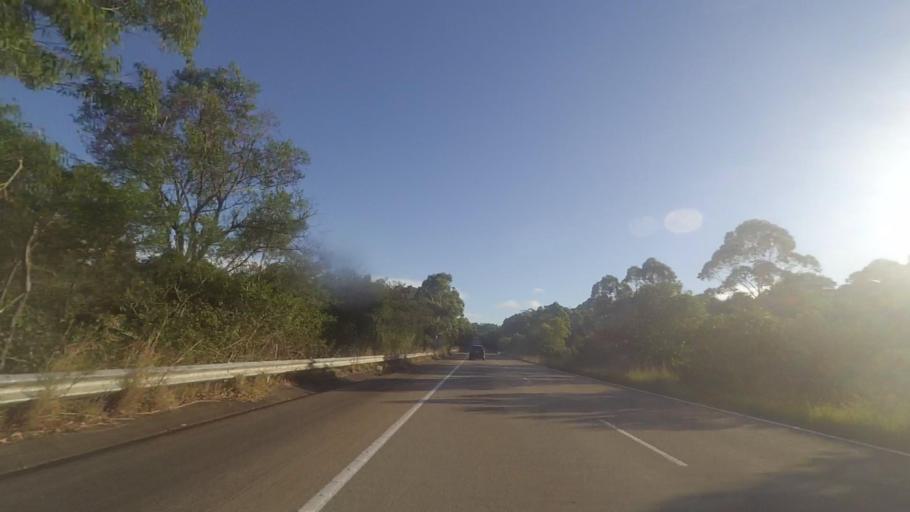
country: AU
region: New South Wales
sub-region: Great Lakes
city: Bulahdelah
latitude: -32.3062
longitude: 152.3455
